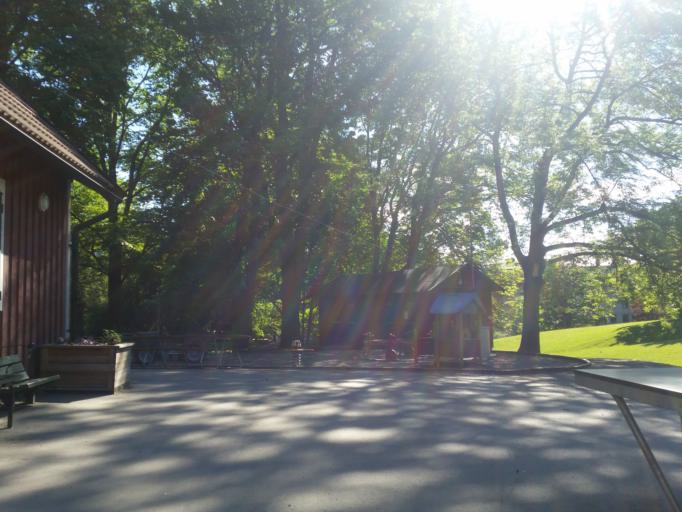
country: SE
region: Stockholm
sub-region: Stockholms Kommun
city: OEstermalm
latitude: 59.3071
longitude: 18.0873
